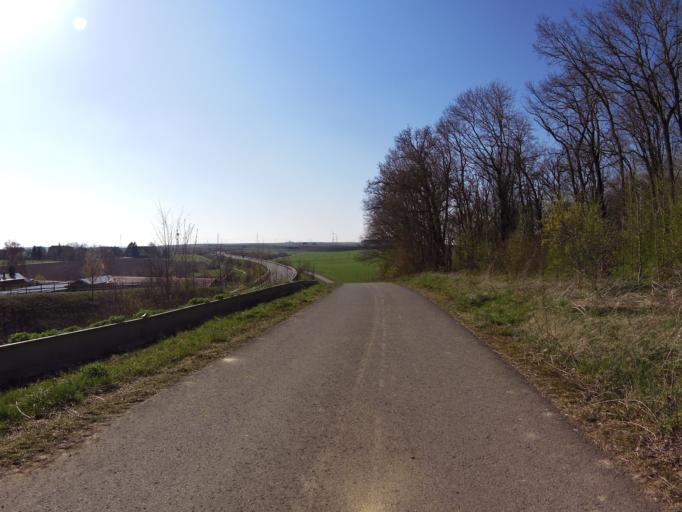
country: DE
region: Bavaria
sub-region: Regierungsbezirk Unterfranken
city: Biebelried
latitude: 49.7682
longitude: 10.0859
